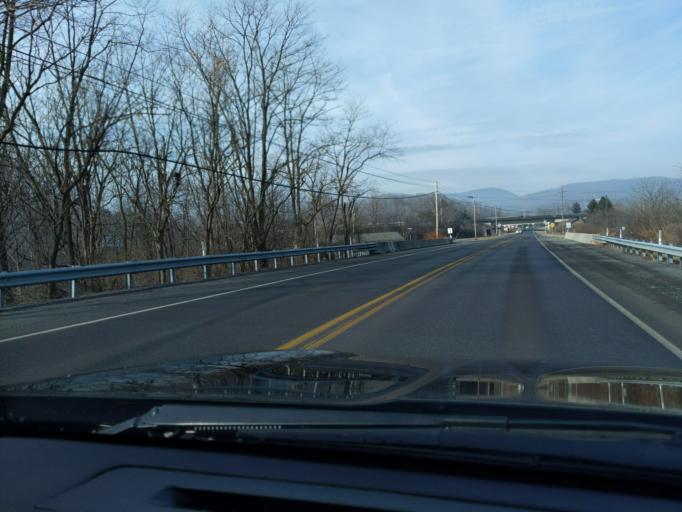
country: US
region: Pennsylvania
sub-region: Blair County
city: Duncansville
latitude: 40.4399
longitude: -78.4219
